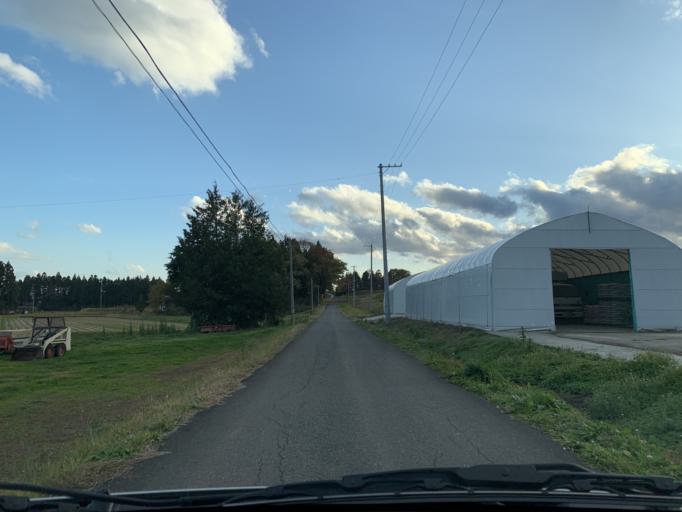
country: JP
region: Iwate
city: Mizusawa
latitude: 39.1053
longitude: 141.0395
